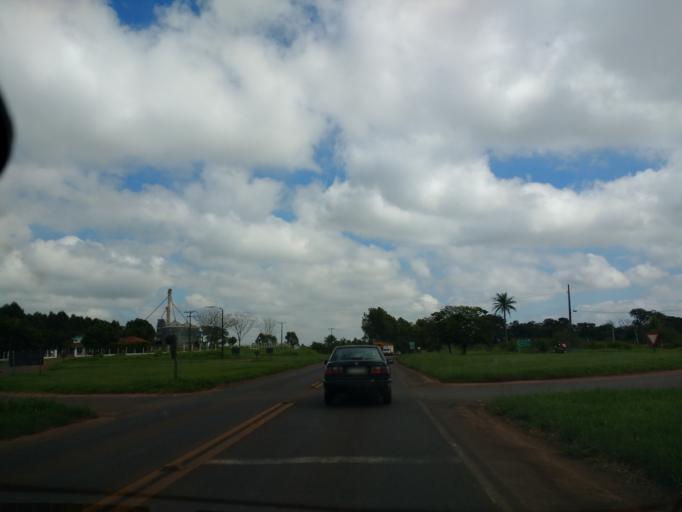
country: BR
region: Parana
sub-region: Cruzeiro Do Oeste
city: Cruzeiro do Oeste
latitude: -23.7987
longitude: -53.0560
